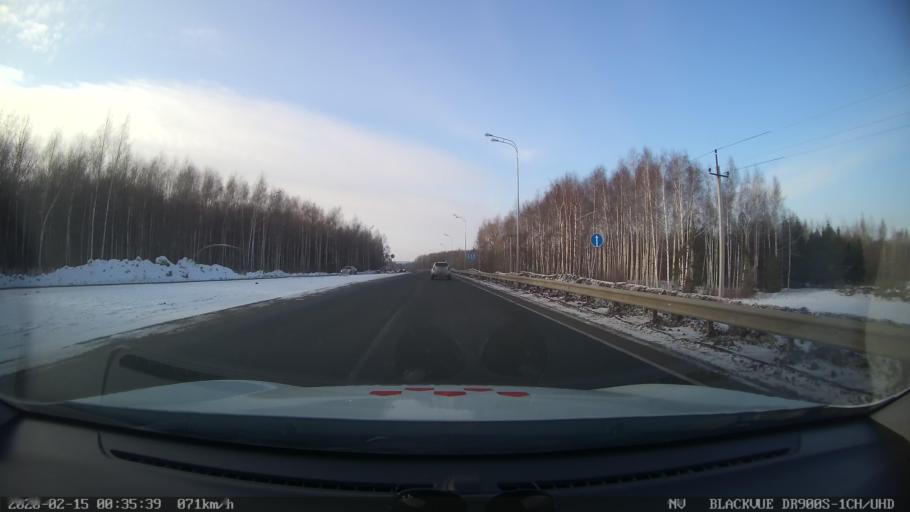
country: RU
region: Tatarstan
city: Verkhniy Uslon
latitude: 55.7100
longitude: 48.8887
